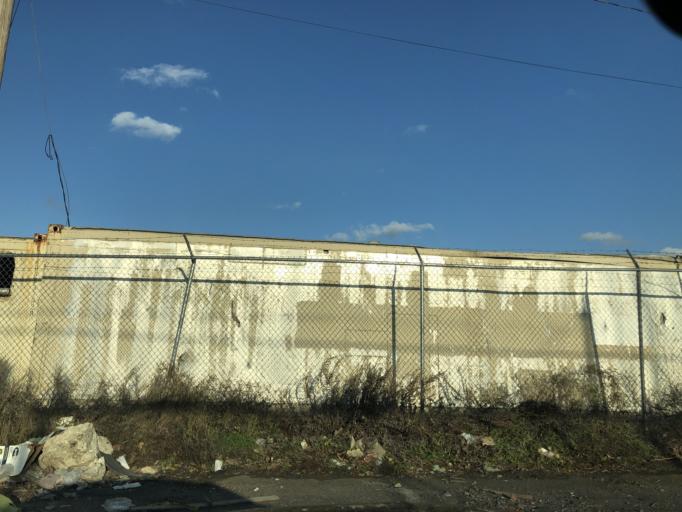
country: US
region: New Jersey
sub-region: Camden County
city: Merchantville
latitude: 39.9804
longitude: -75.0921
